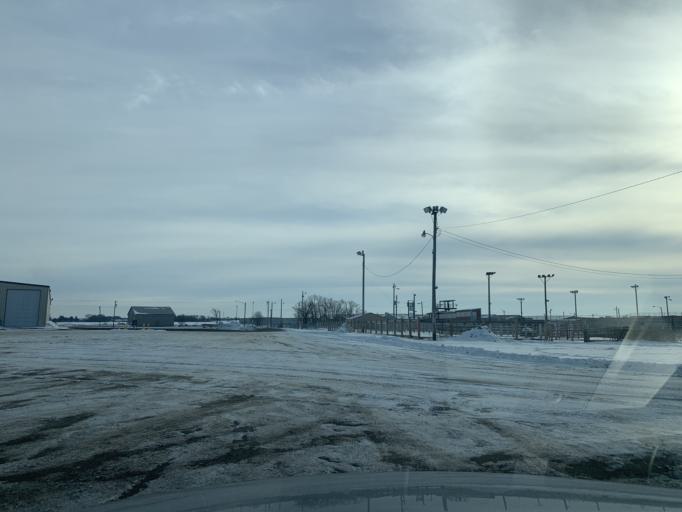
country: US
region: Minnesota
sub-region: Wright County
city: Buffalo
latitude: 45.1610
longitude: -93.8503
